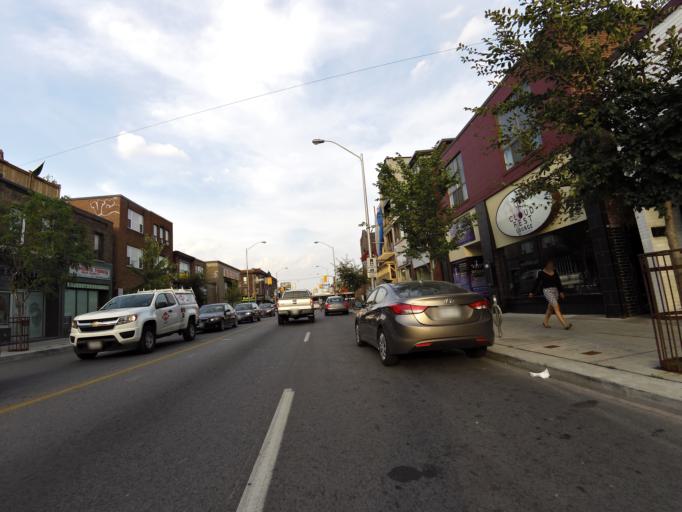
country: CA
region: Ontario
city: Toronto
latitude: 43.6617
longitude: -79.4266
